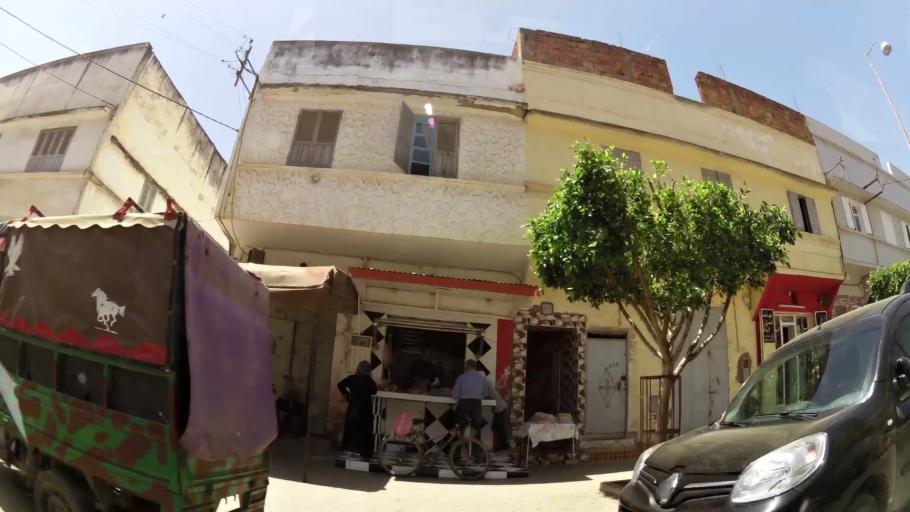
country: MA
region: Rabat-Sale-Zemmour-Zaer
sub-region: Khemisset
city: Khemisset
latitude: 33.8319
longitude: -6.0749
